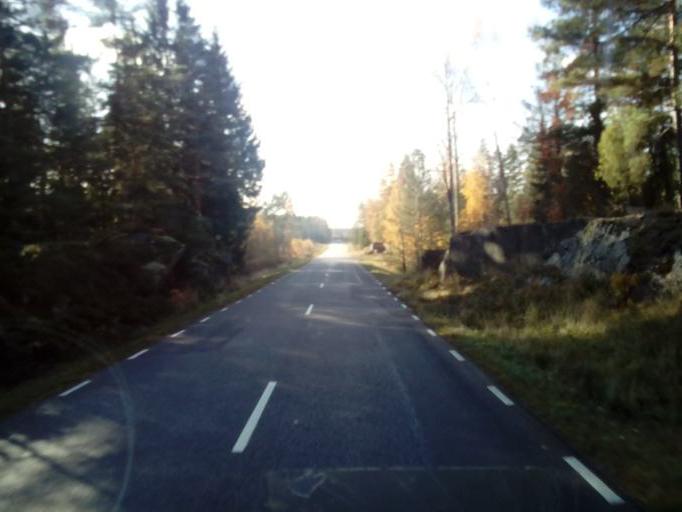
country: SE
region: Kalmar
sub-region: Vasterviks Kommun
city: Ankarsrum
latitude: 57.7475
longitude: 16.1132
